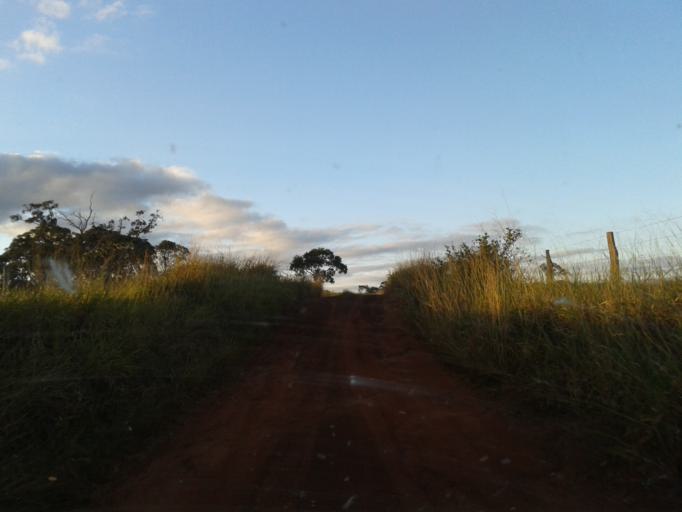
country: BR
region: Minas Gerais
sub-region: Campina Verde
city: Campina Verde
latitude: -19.4984
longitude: -49.6798
